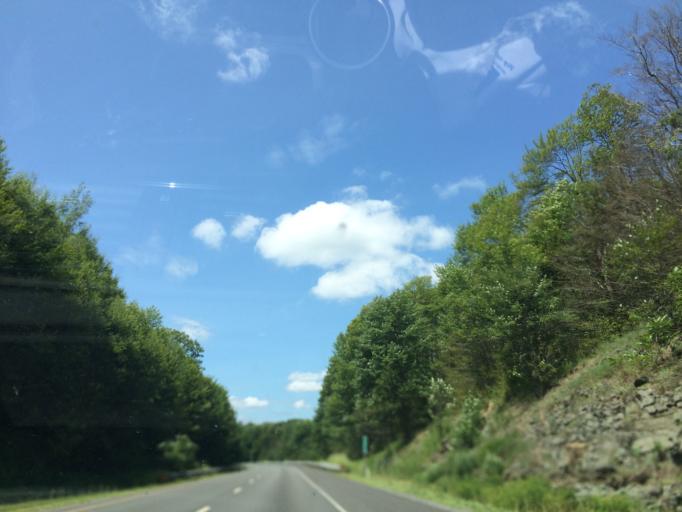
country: US
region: Pennsylvania
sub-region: Wayne County
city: Hawley
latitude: 41.3479
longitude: -75.2766
